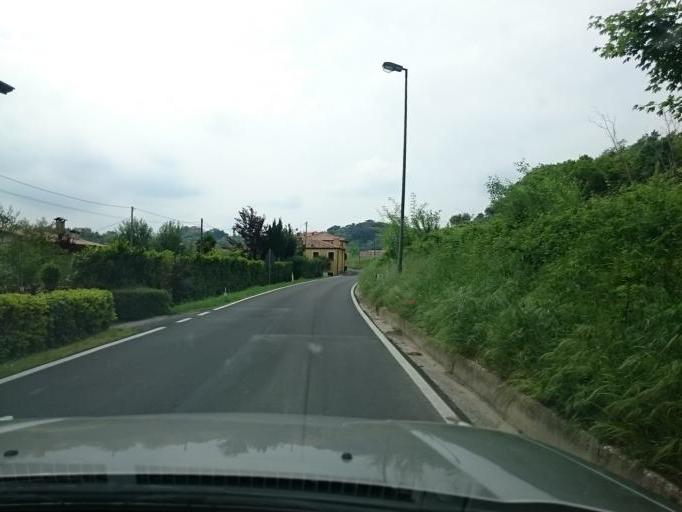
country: IT
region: Veneto
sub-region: Provincia di Padova
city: Arqua Petrarca
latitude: 45.2697
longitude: 11.7369
